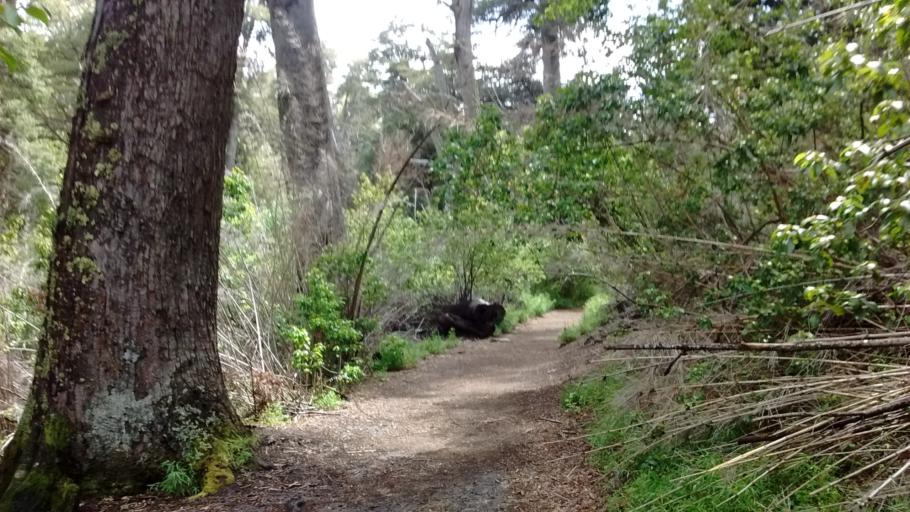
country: AR
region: Rio Negro
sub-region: Departamento de Bariloche
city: San Carlos de Bariloche
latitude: -41.0583
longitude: -71.5656
